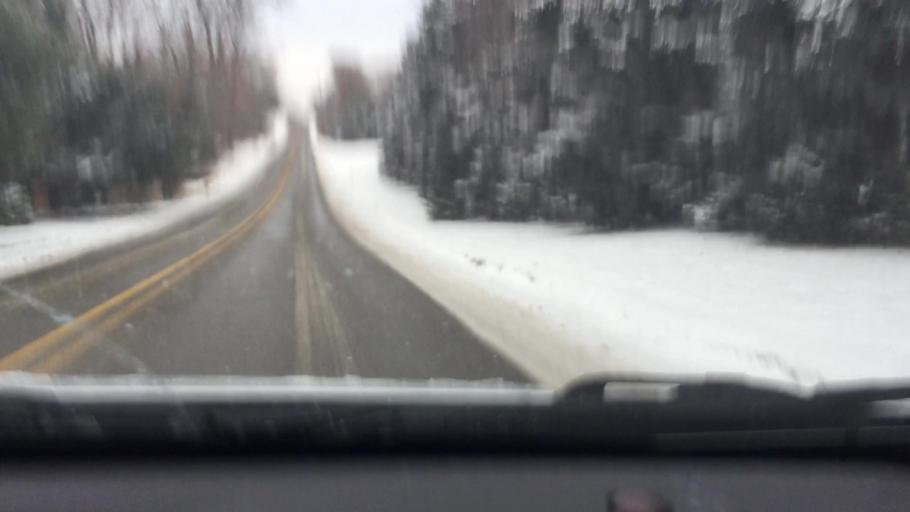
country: US
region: Pennsylvania
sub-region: Butler County
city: Fernway
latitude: 40.7245
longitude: -80.1214
